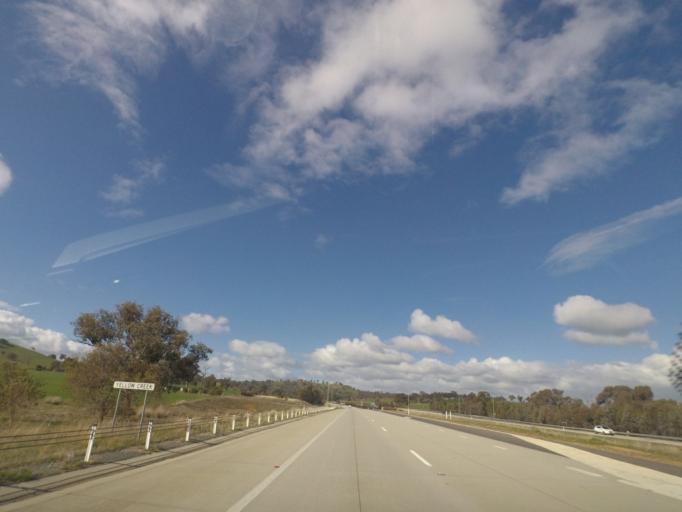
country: AU
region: New South Wales
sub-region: Albury Municipality
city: Lavington
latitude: -35.9264
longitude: 147.0757
